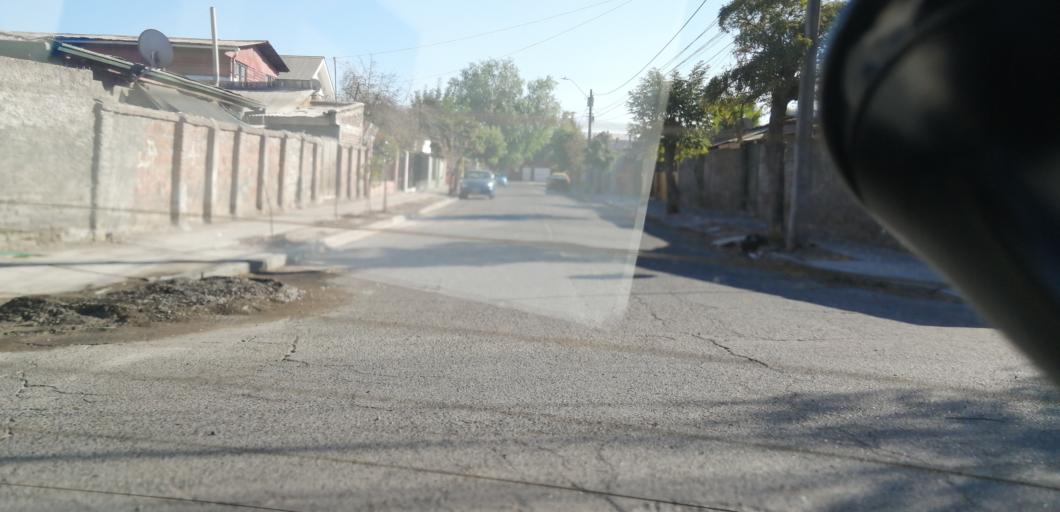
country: CL
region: Santiago Metropolitan
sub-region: Provincia de Santiago
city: Lo Prado
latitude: -33.4373
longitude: -70.7623
